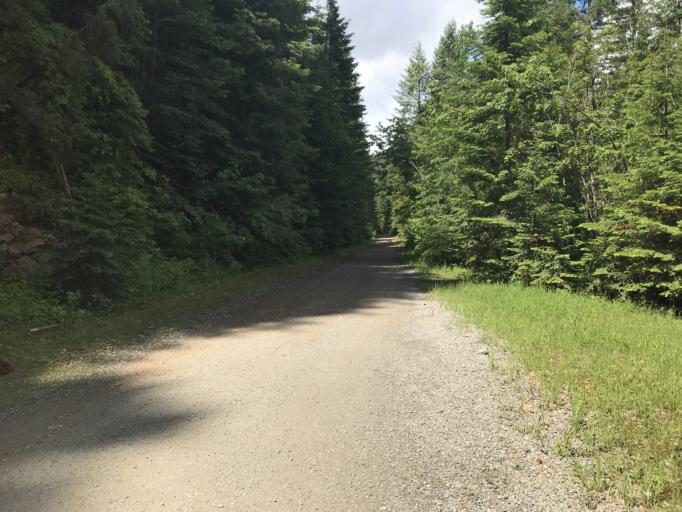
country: US
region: Idaho
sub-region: Shoshone County
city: Wallace
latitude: 47.3530
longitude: -115.6552
